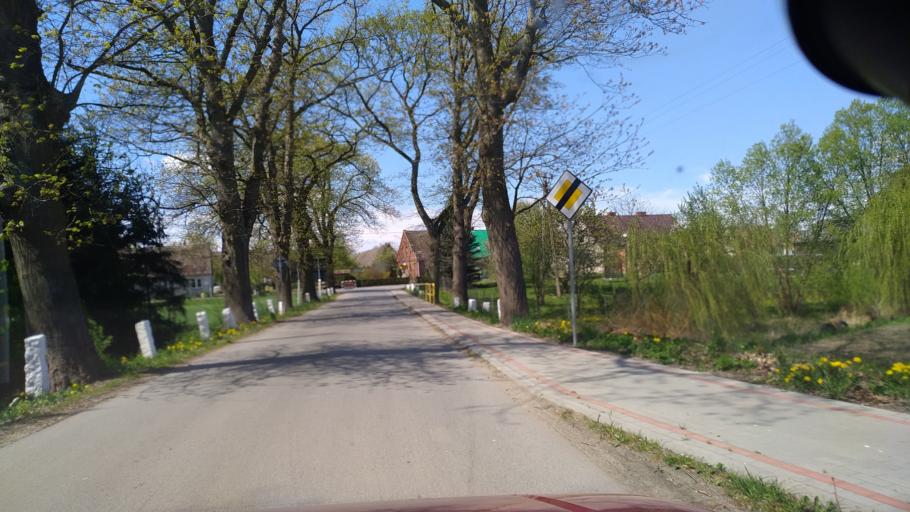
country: PL
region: Greater Poland Voivodeship
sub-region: Powiat zlotowski
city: Tarnowka
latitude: 53.2665
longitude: 16.9030
